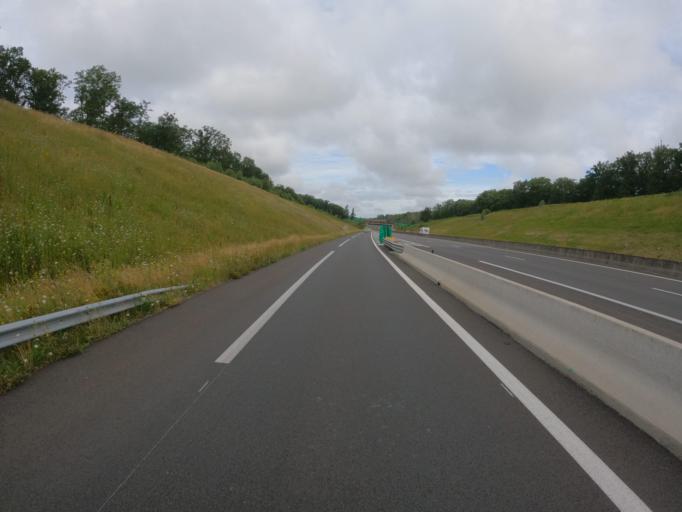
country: FR
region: Centre
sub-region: Departement d'Indre-et-Loire
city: Montbazon
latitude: 47.3032
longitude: 0.6795
